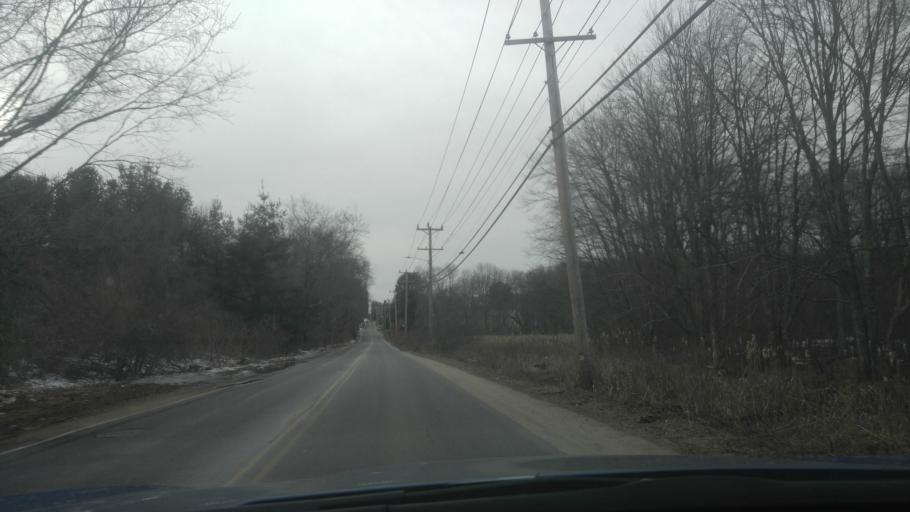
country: US
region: Rhode Island
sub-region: Kent County
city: West Warwick
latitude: 41.6736
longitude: -71.5048
